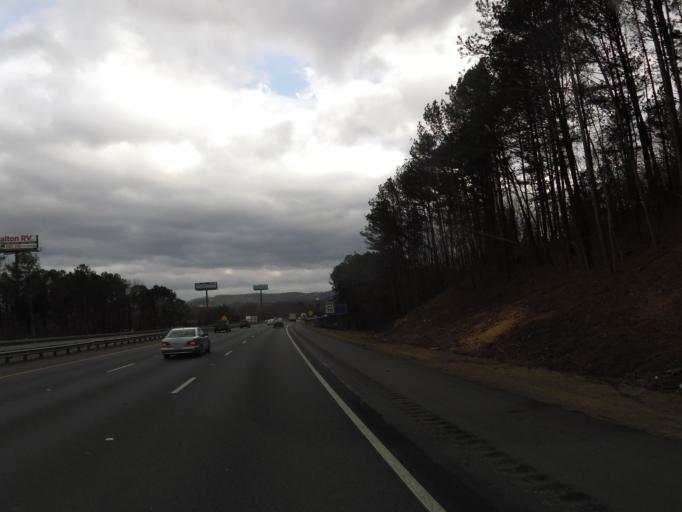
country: US
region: Georgia
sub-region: Catoosa County
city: Indian Springs
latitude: 34.9644
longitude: -85.1866
